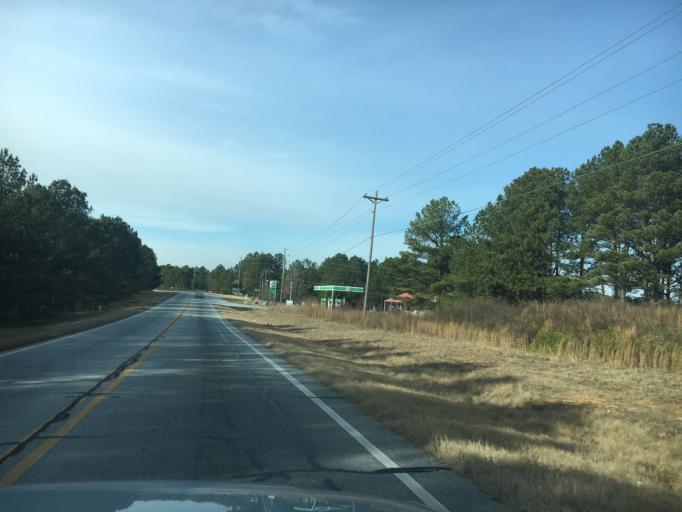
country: US
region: Georgia
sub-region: Jackson County
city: Hoschton
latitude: 34.0856
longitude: -83.7445
